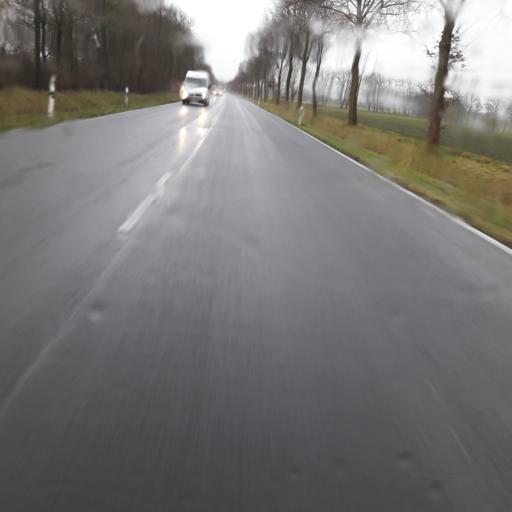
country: DE
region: North Rhine-Westphalia
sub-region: Regierungsbezirk Detmold
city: Petershagen
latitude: 52.4016
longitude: 8.9536
